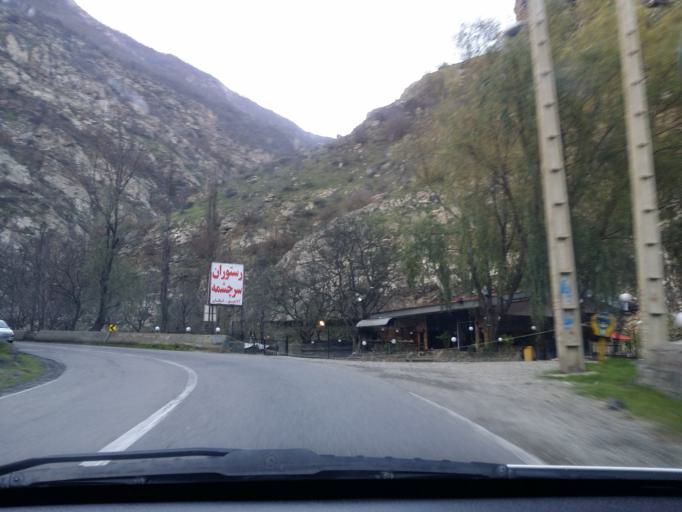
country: IR
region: Mazandaran
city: Chalus
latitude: 36.3021
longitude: 51.2470
